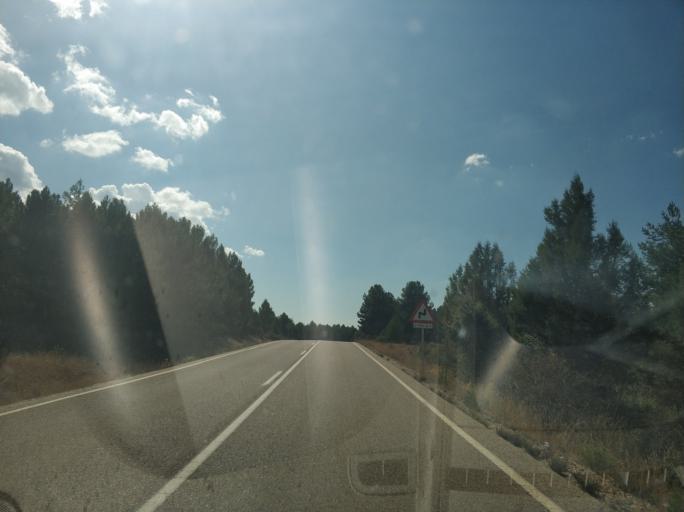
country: ES
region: Castille and Leon
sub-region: Provincia de Soria
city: Herrera de Soria
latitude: 41.7680
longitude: -3.0307
